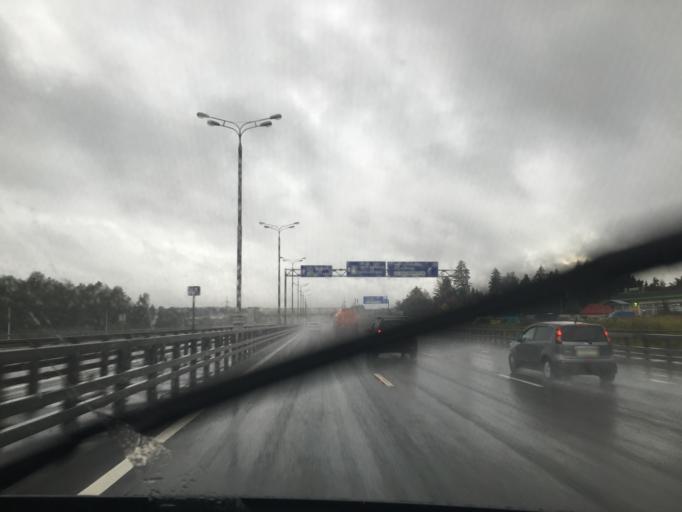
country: RU
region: Moskovskaya
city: Aprelevka
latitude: 55.5273
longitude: 37.0317
